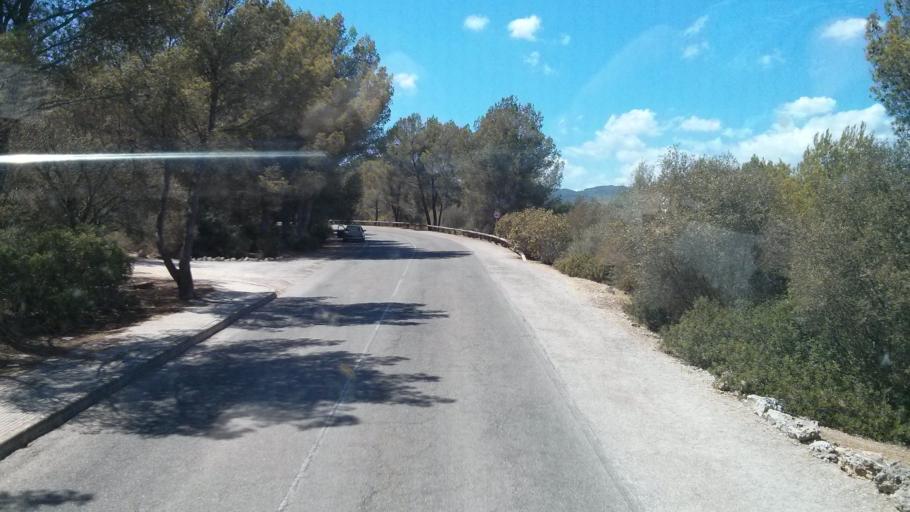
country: ES
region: Balearic Islands
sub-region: Illes Balears
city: Palma
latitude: 39.5693
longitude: 2.6227
